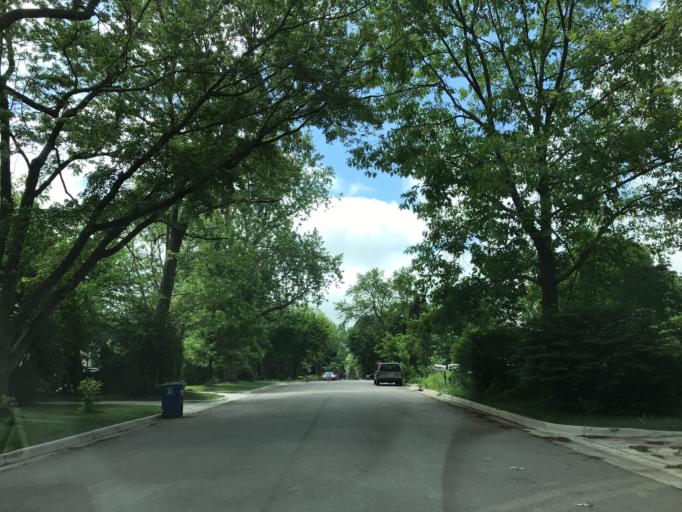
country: US
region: Michigan
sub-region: Washtenaw County
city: Ann Arbor
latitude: 42.2430
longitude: -83.7037
